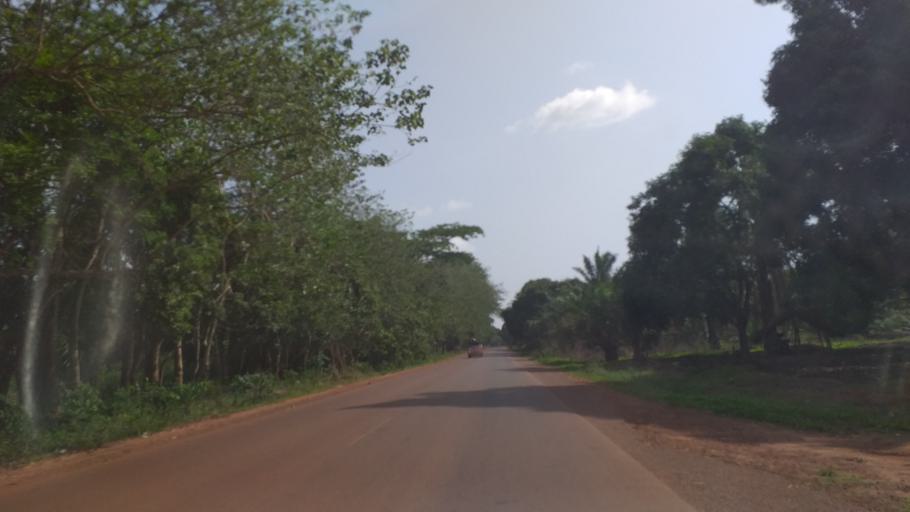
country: GN
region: Boke
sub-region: Boke Prefecture
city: Sangueya
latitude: 10.8190
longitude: -14.3765
